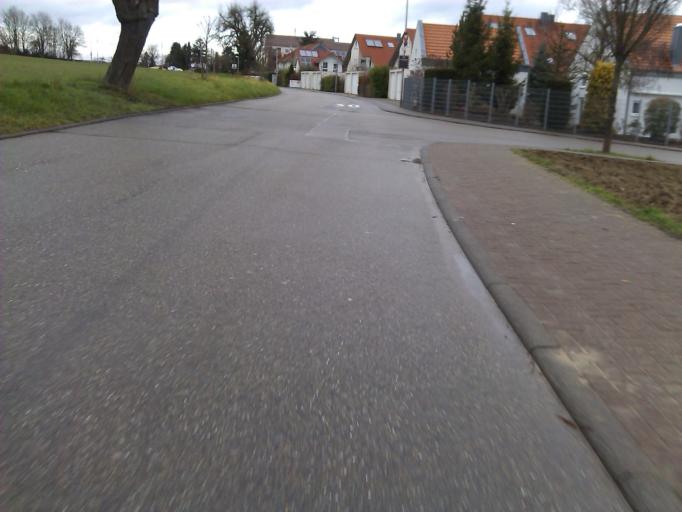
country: DE
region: Baden-Wuerttemberg
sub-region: Regierungsbezirk Stuttgart
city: Bad Wimpfen
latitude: 49.2255
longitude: 9.1491
